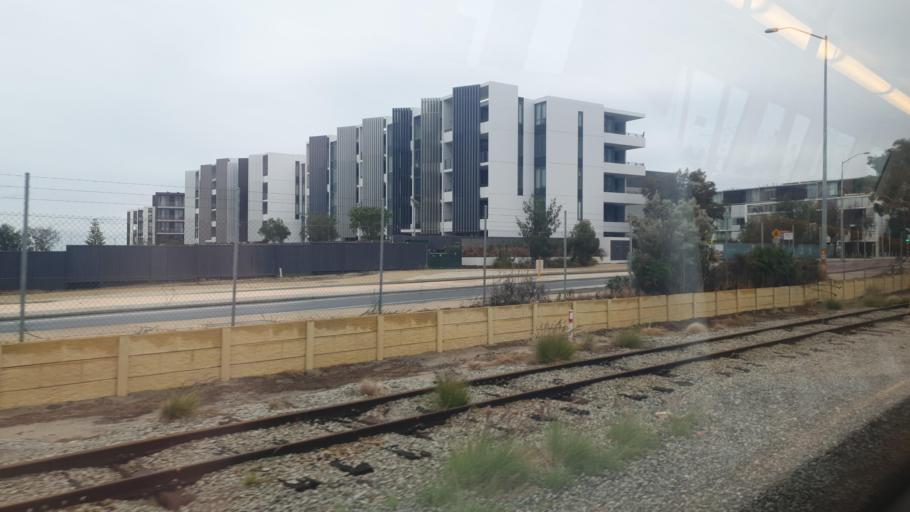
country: AU
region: Western Australia
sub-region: Fremantle
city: North Fremantle
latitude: -32.0307
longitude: 115.7517
